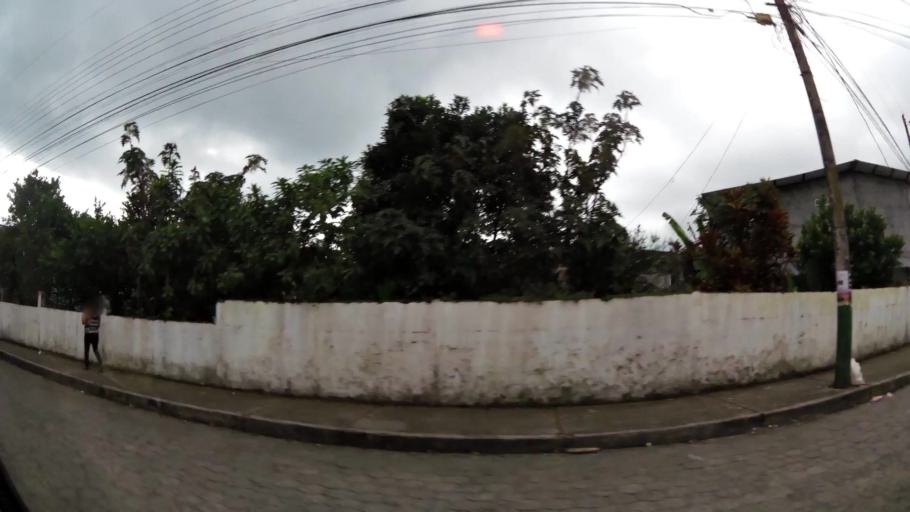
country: EC
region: Pastaza
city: Puyo
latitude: -1.4860
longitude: -78.0038
